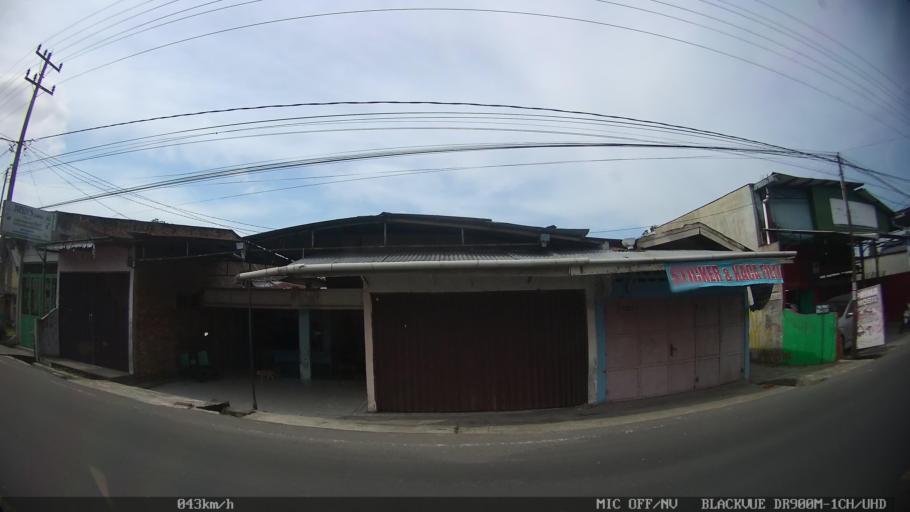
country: ID
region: North Sumatra
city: Percut
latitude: 3.6072
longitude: 98.7721
